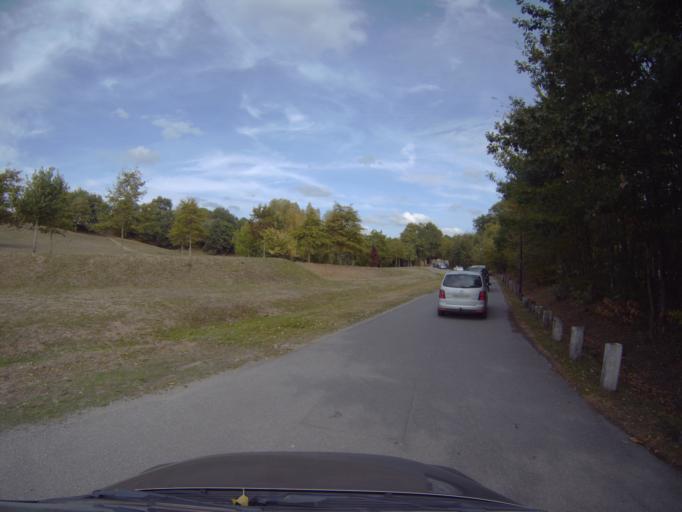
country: FR
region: Pays de la Loire
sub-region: Departement de la Loire-Atlantique
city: Saint-Herblain
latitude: 47.2107
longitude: -1.6347
